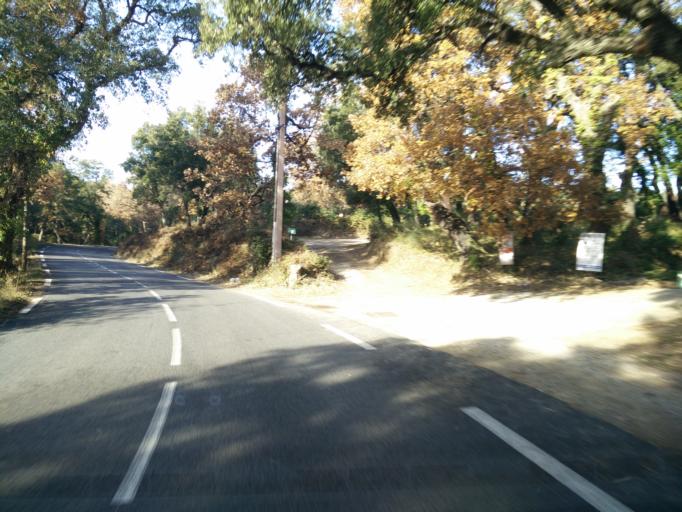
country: FR
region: Provence-Alpes-Cote d'Azur
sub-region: Departement du Var
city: La Garde-Freinet
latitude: 43.3268
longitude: 6.4720
